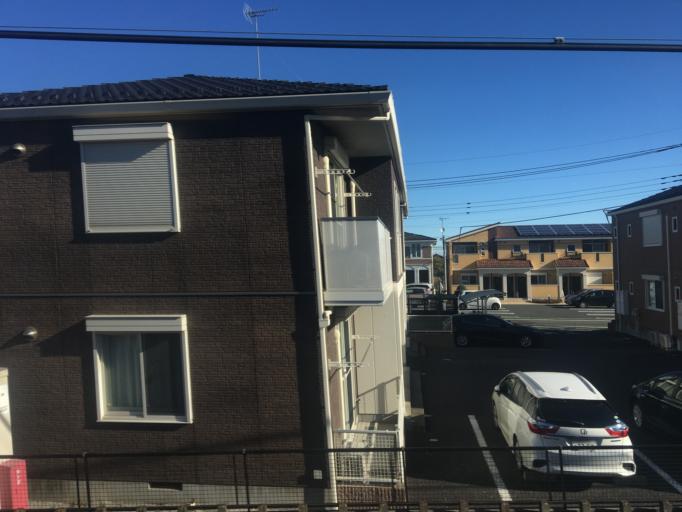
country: JP
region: Saitama
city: Sakado
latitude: 35.9347
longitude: 139.4273
